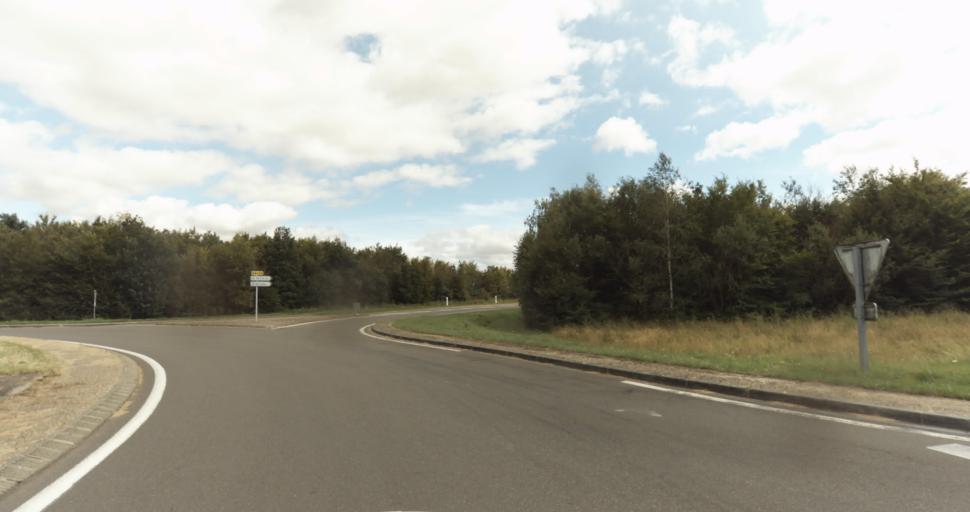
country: FR
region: Haute-Normandie
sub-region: Departement de l'Eure
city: Damville
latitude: 48.8878
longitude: 1.1764
